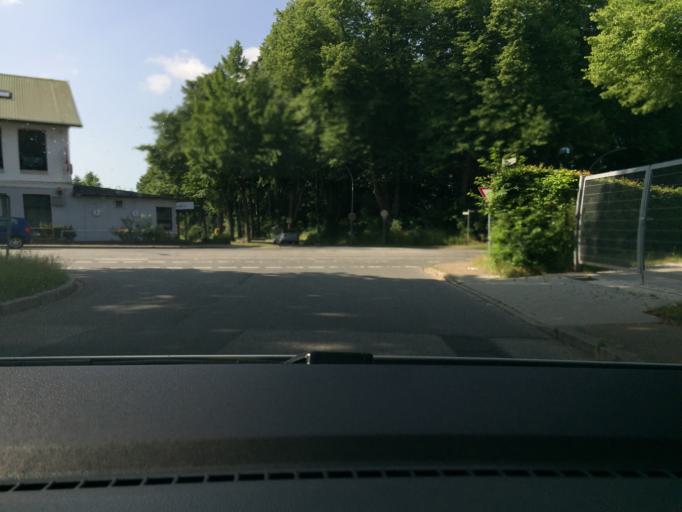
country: DE
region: Schleswig-Holstein
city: Itzehoe
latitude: 53.9316
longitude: 9.5384
